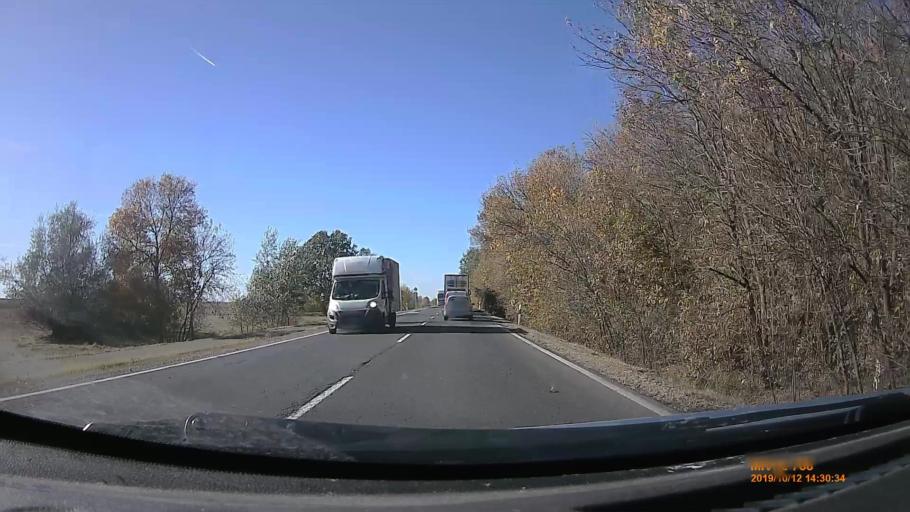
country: HU
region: Hajdu-Bihar
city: Berettyoujfalu
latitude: 47.1762
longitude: 21.5949
